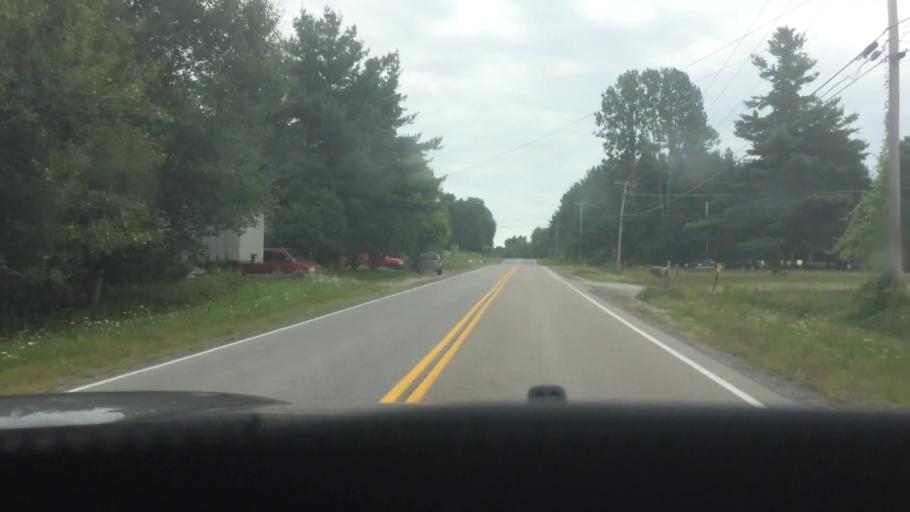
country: US
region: New York
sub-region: St. Lawrence County
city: Hannawa Falls
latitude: 44.5377
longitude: -75.0188
